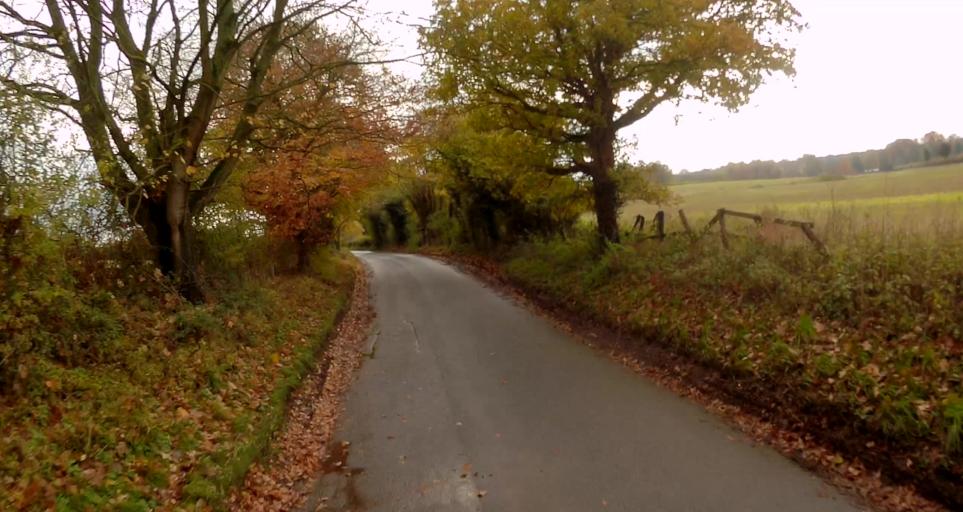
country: GB
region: England
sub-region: Hampshire
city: Old Basing
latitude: 51.2349
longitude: -1.0292
